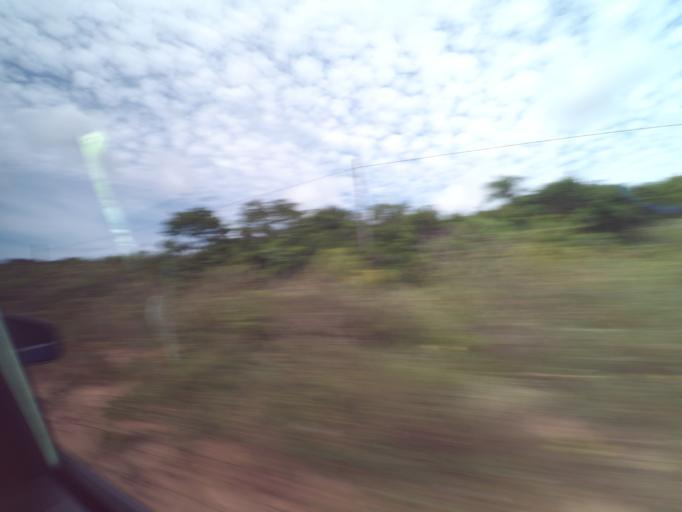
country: BO
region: Santa Cruz
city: Santa Cruz de la Sierra
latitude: -17.9209
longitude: -63.1605
